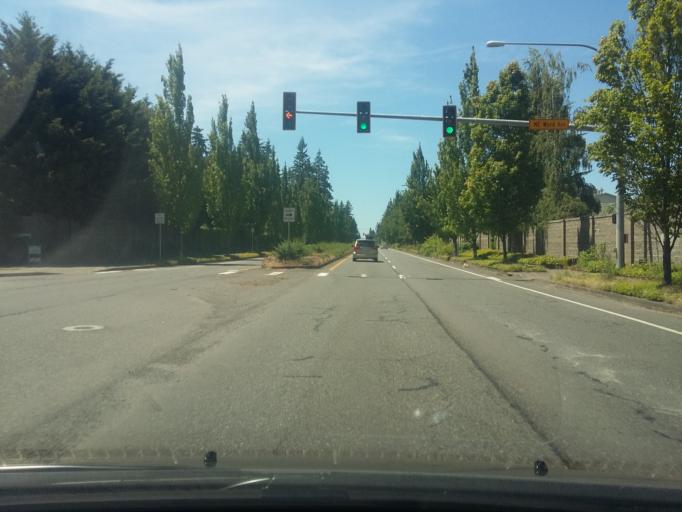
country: US
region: Washington
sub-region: Clark County
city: Mill Plain
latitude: 45.6829
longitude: -122.5113
